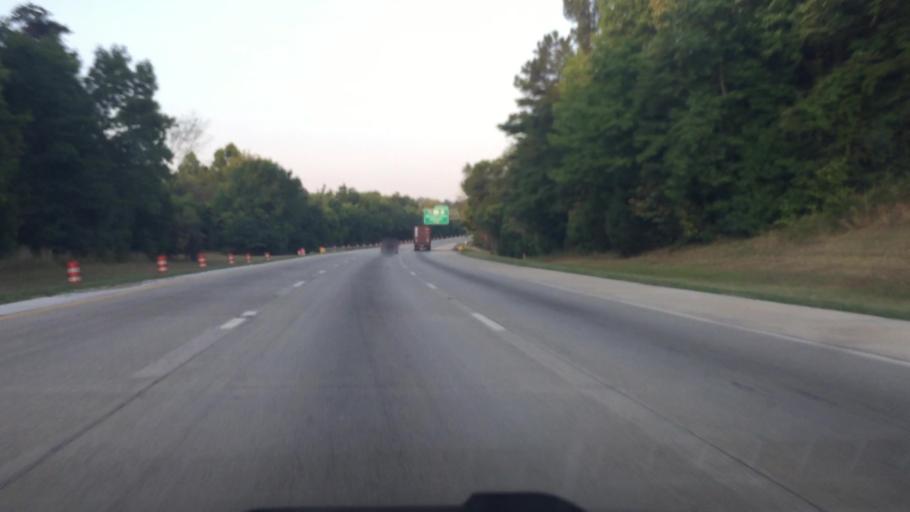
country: US
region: North Carolina
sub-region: Guilford County
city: Jamestown
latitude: 35.9419
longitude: -79.9048
